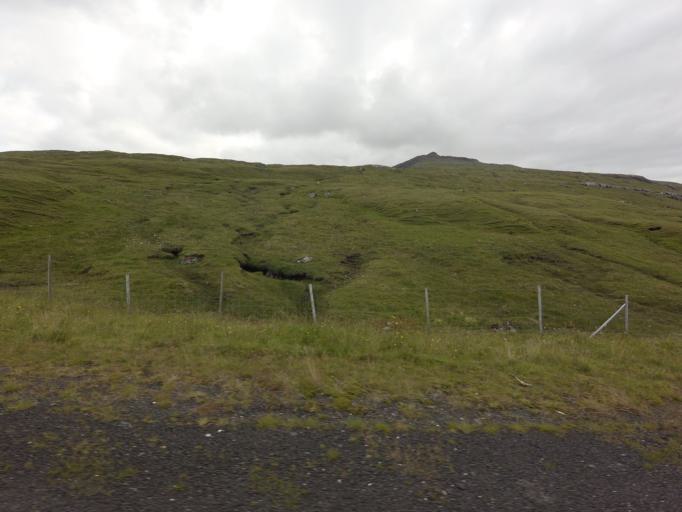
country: FO
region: Eysturoy
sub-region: Eidi
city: Eidi
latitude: 62.2142
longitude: -6.9966
